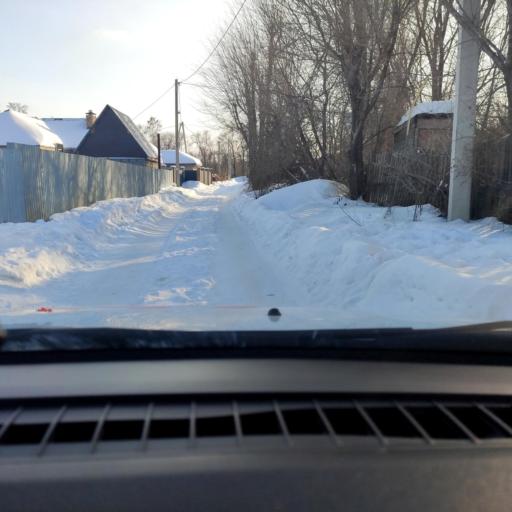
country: RU
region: Samara
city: Samara
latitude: 53.1304
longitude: 50.2513
